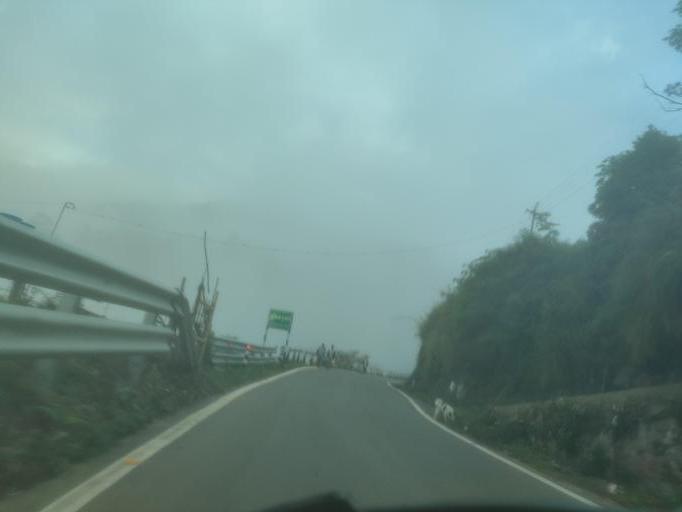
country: IN
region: Tamil Nadu
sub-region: Dindigul
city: Kodaikanal
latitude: 10.3168
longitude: 77.5657
